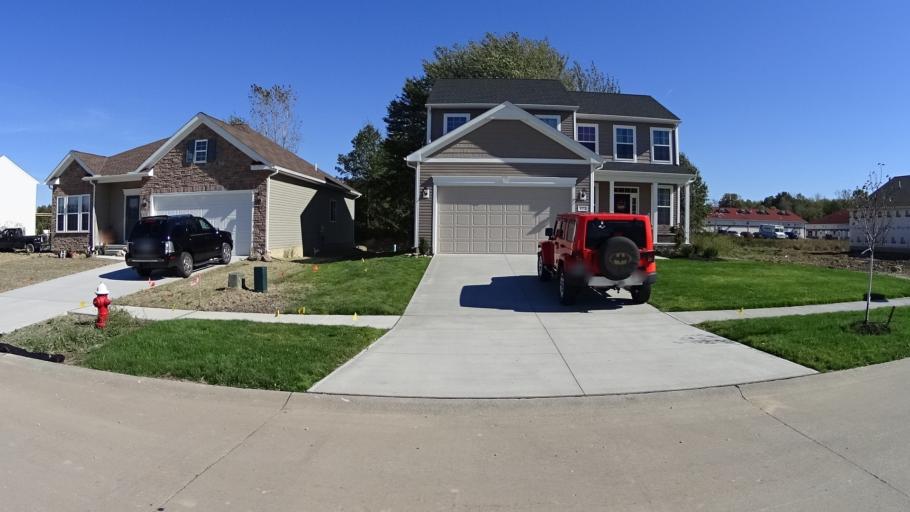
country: US
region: Ohio
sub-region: Lorain County
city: Amherst
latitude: 41.3850
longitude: -82.2125
